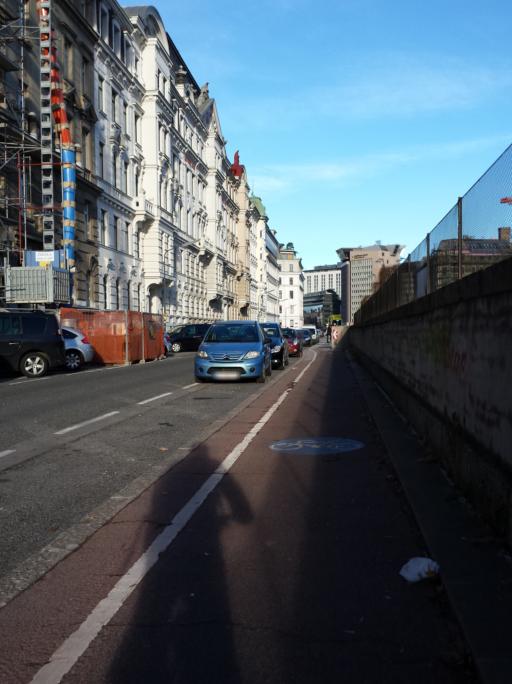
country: AT
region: Vienna
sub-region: Wien Stadt
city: Vienna
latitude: 48.2012
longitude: 16.3844
